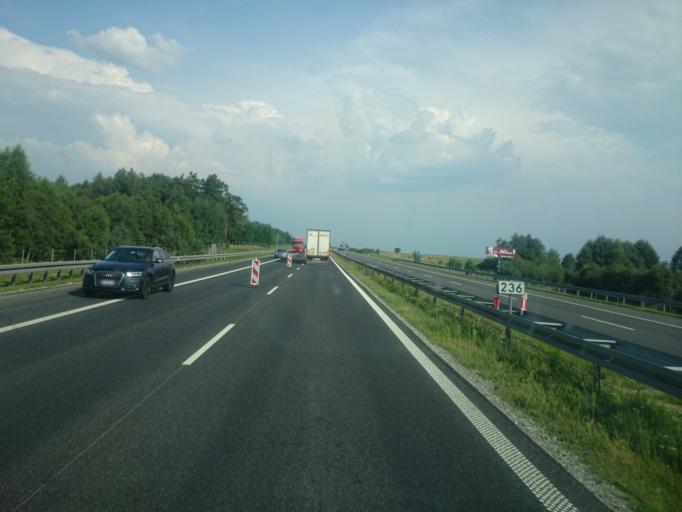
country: PL
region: Opole Voivodeship
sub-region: Powiat opolski
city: Proszkow
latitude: 50.5806
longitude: 17.8338
